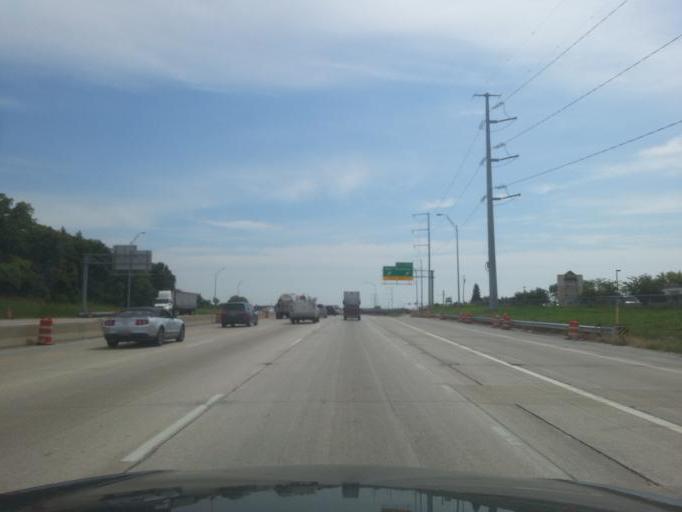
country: US
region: Wisconsin
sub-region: Dane County
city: Monona
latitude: 43.0437
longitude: -89.3601
